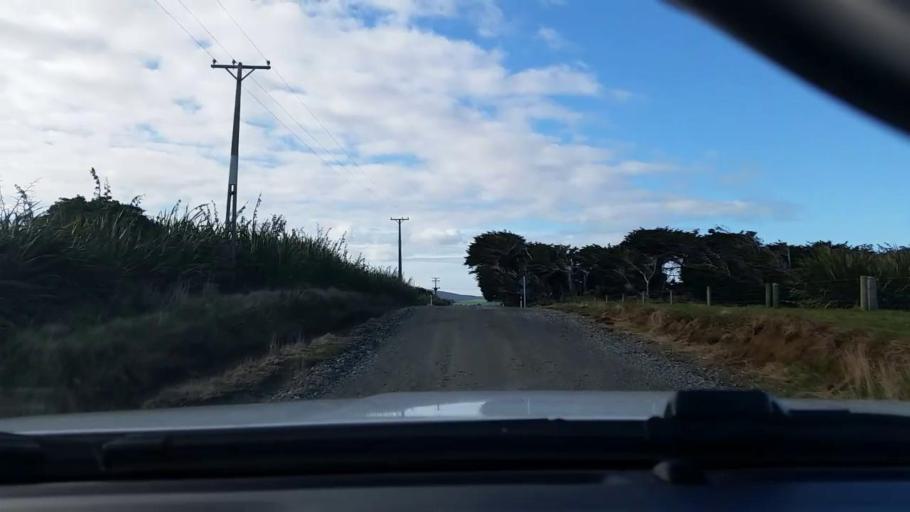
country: NZ
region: Southland
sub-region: Southland District
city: Riverton
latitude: -46.3303
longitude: 167.7136
